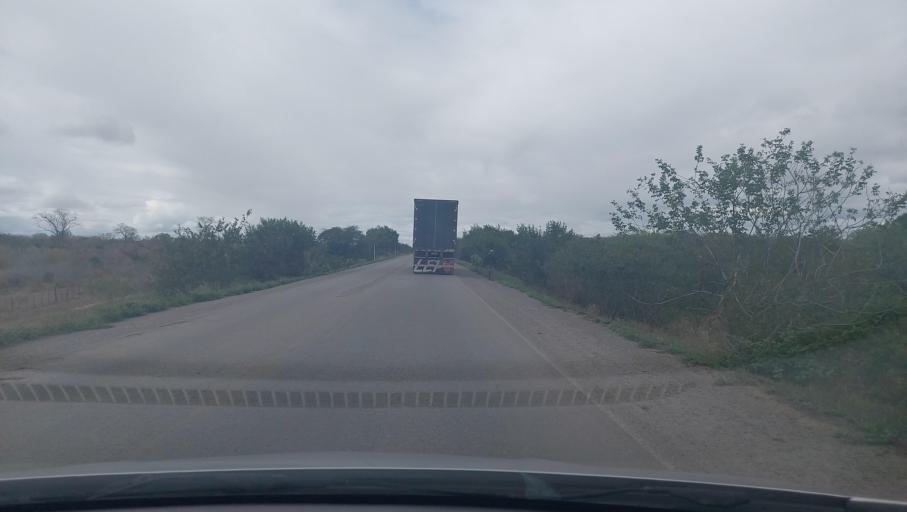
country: BR
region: Bahia
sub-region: Itaberaba
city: Itaberaba
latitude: -12.5136
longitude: -39.9327
